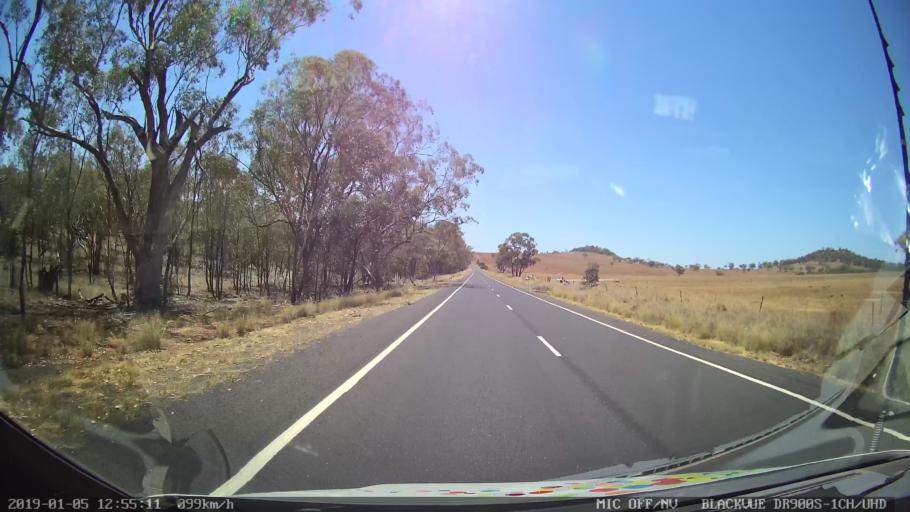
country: AU
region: New South Wales
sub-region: Warrumbungle Shire
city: Coonabarabran
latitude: -31.1192
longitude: 149.7013
